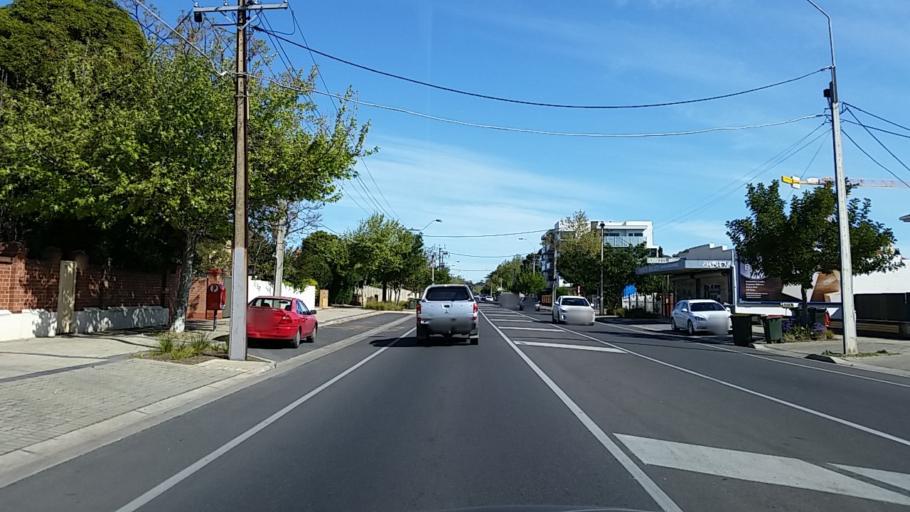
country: AU
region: South Australia
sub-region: Prospect
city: Prospect
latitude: -34.8909
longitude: 138.5853
